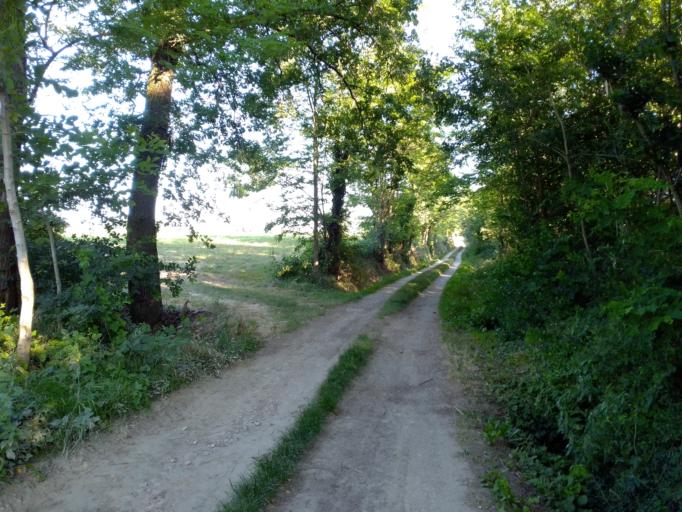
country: IT
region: Emilia-Romagna
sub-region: Provincia di Piacenza
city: Borgonovo Valtidone
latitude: 45.0035
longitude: 9.4332
